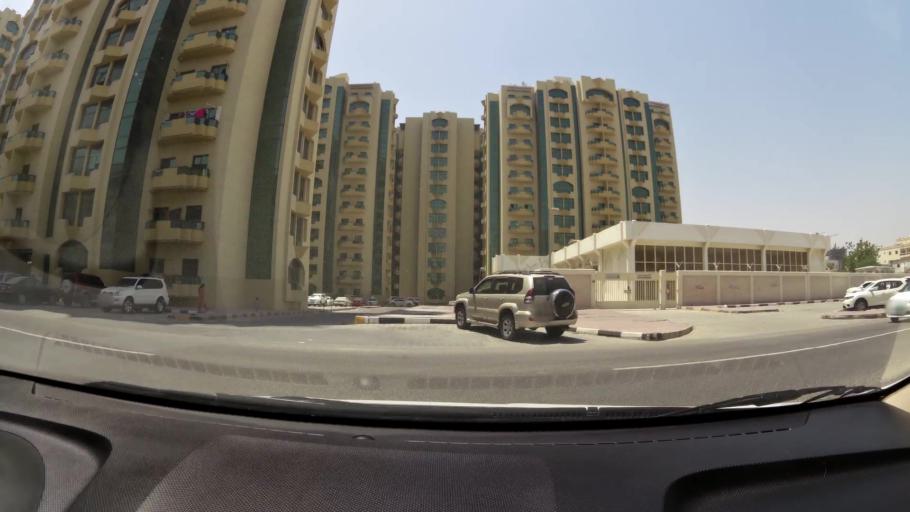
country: AE
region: Ajman
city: Ajman
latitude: 25.3956
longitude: 55.4504
